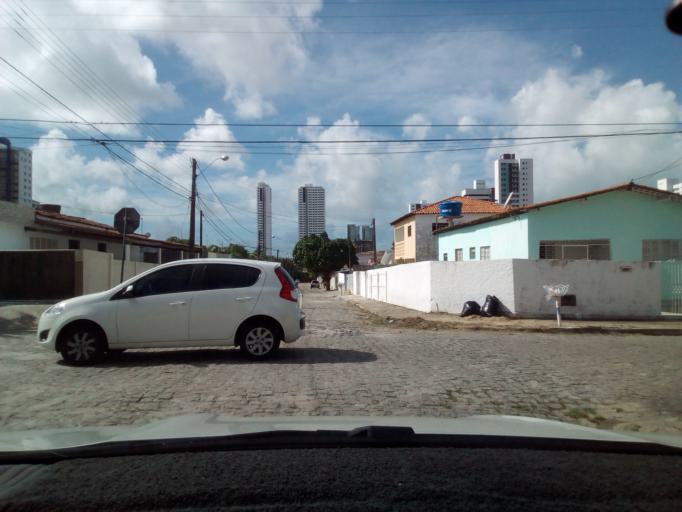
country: BR
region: Paraiba
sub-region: Joao Pessoa
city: Joao Pessoa
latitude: -7.1166
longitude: -34.8488
